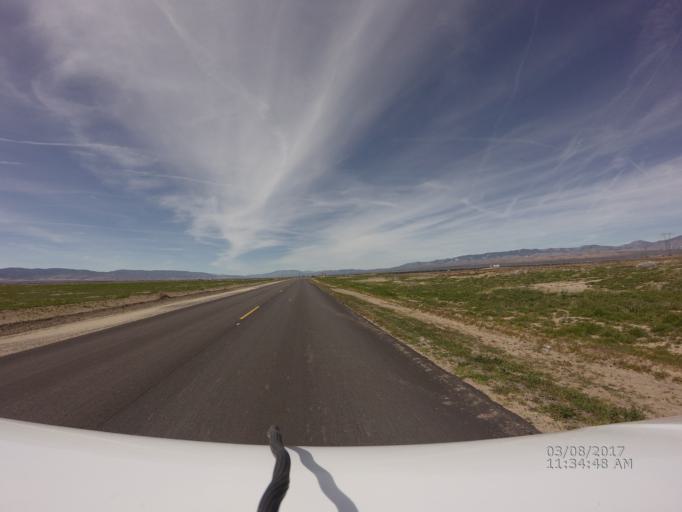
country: US
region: California
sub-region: Los Angeles County
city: Green Valley
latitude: 34.8189
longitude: -118.4123
